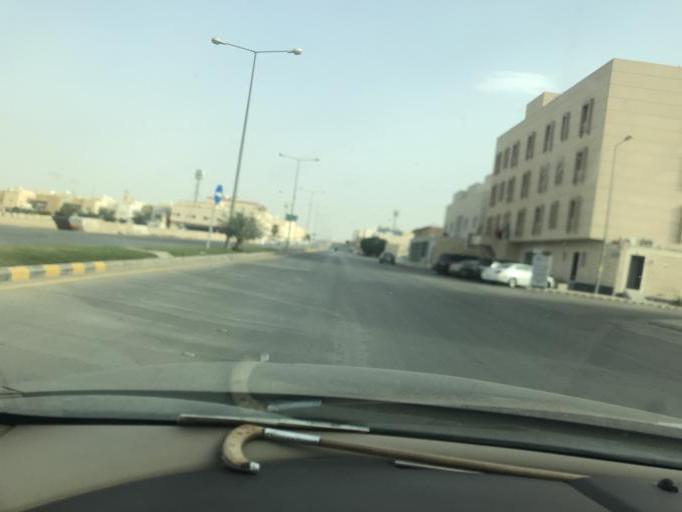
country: SA
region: Ar Riyad
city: Riyadh
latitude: 24.7862
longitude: 46.7133
